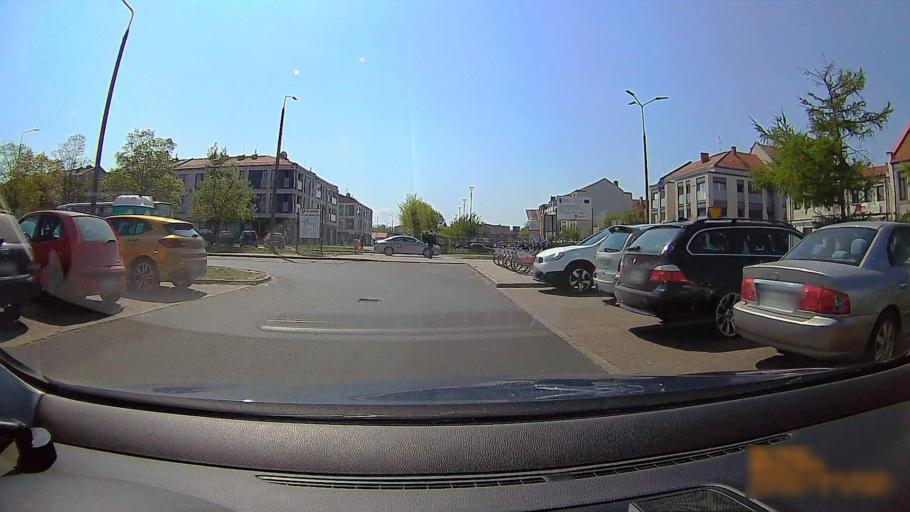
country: PL
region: Greater Poland Voivodeship
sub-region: Konin
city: Konin
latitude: 52.2099
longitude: 18.2572
